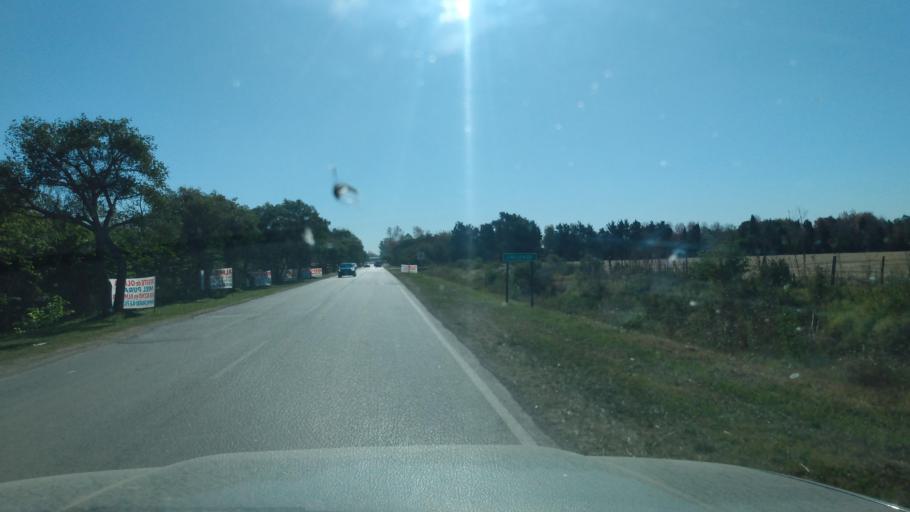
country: AR
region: Buenos Aires
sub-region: Partido de Lujan
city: Lujan
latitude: -34.4907
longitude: -59.2111
